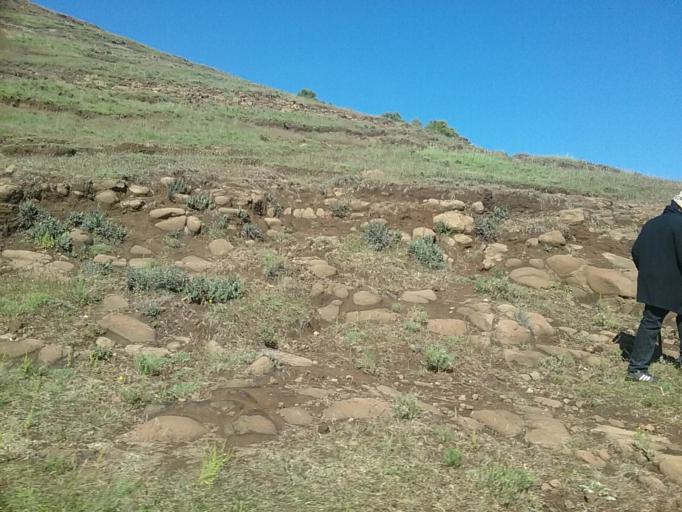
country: LS
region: Berea
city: Teyateyaneng
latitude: -29.2326
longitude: 27.9240
